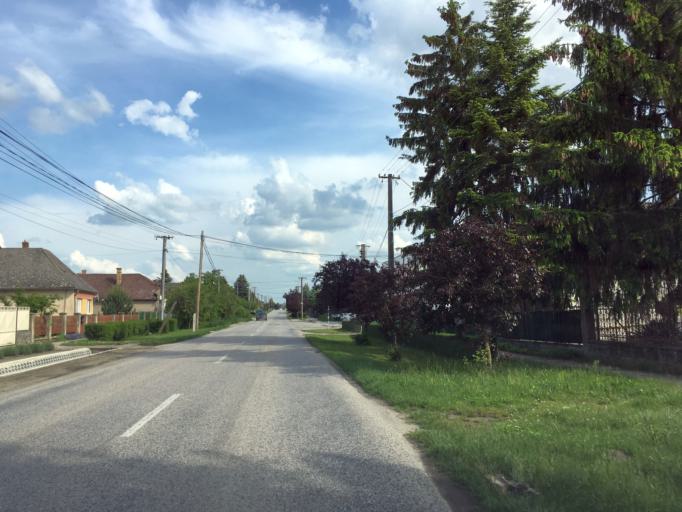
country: SK
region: Nitriansky
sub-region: Okres Komarno
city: Hurbanovo
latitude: 47.8058
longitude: 18.2309
